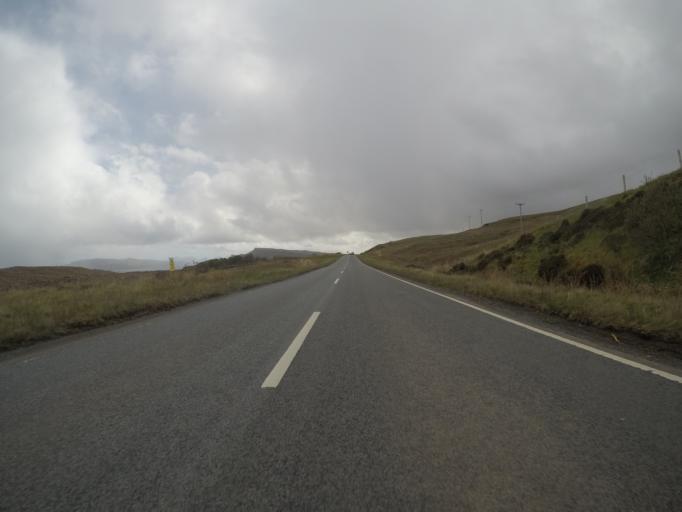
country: GB
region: Scotland
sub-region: Highland
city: Portree
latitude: 57.5053
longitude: -6.1522
